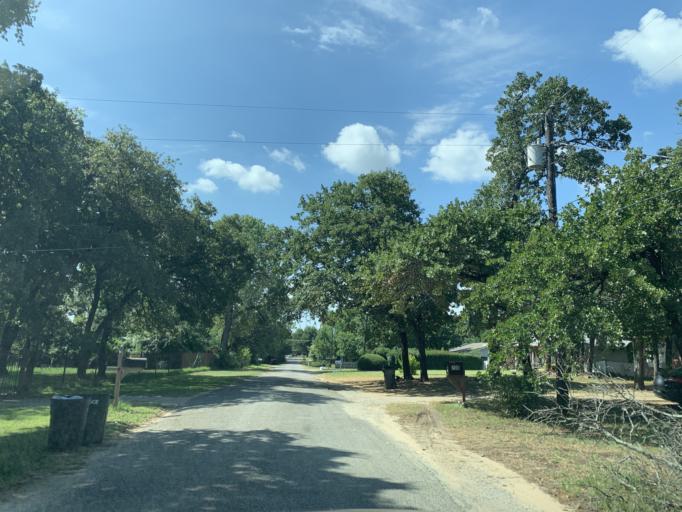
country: US
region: Texas
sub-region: Tarrant County
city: Azle
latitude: 32.8823
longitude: -97.5401
